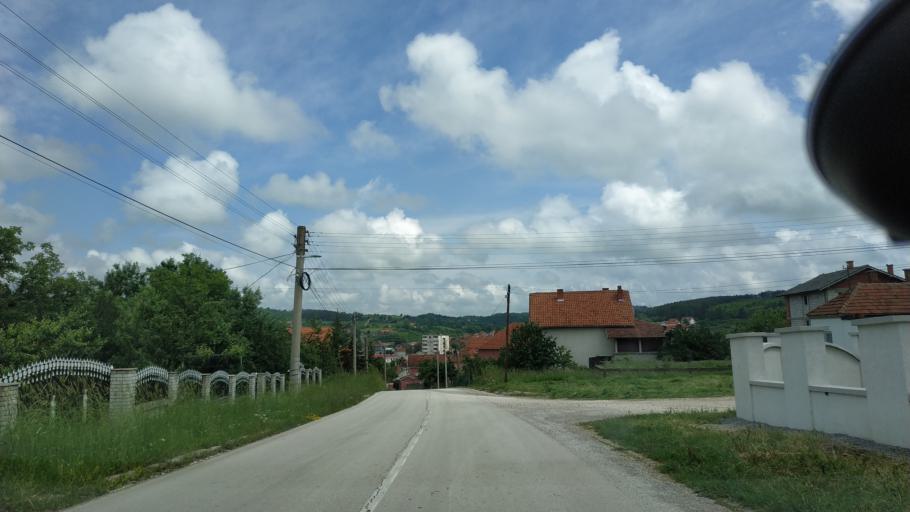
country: RS
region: Central Serbia
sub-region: Zajecarski Okrug
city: Boljevac
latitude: 43.8266
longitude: 21.9581
